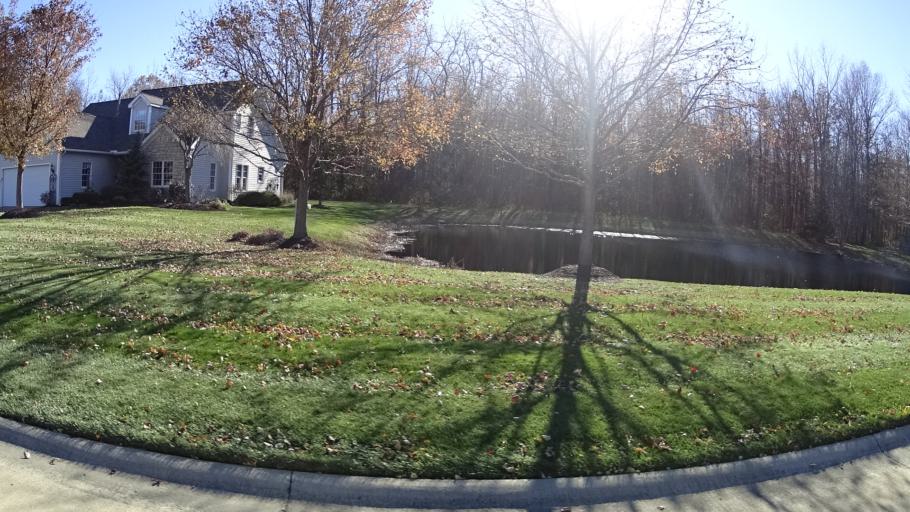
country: US
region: Ohio
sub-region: Lorain County
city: Avon Center
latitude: 41.4327
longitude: -81.9984
